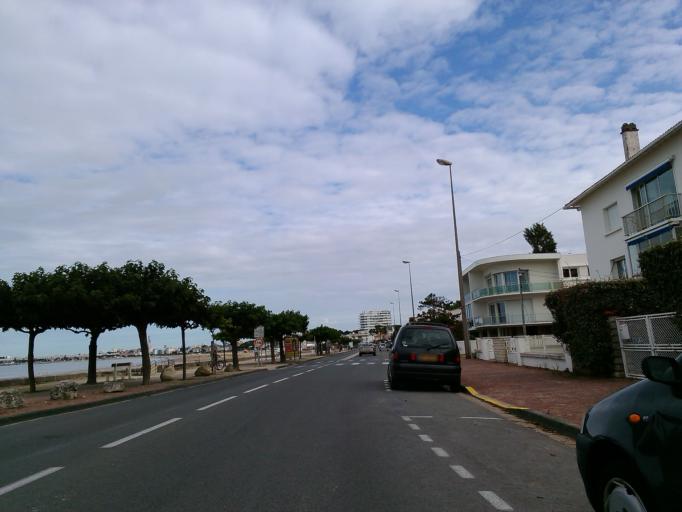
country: FR
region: Poitou-Charentes
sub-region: Departement de la Charente-Maritime
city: Saint-Georges-de-Didonne
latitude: 45.6085
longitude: -1.0085
